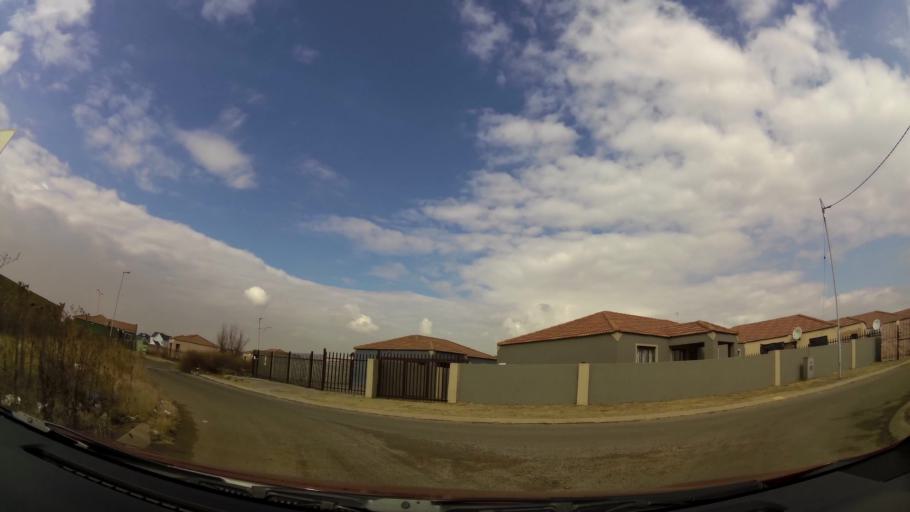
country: ZA
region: Gauteng
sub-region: Sedibeng District Municipality
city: Vanderbijlpark
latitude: -26.7154
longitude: 27.8860
